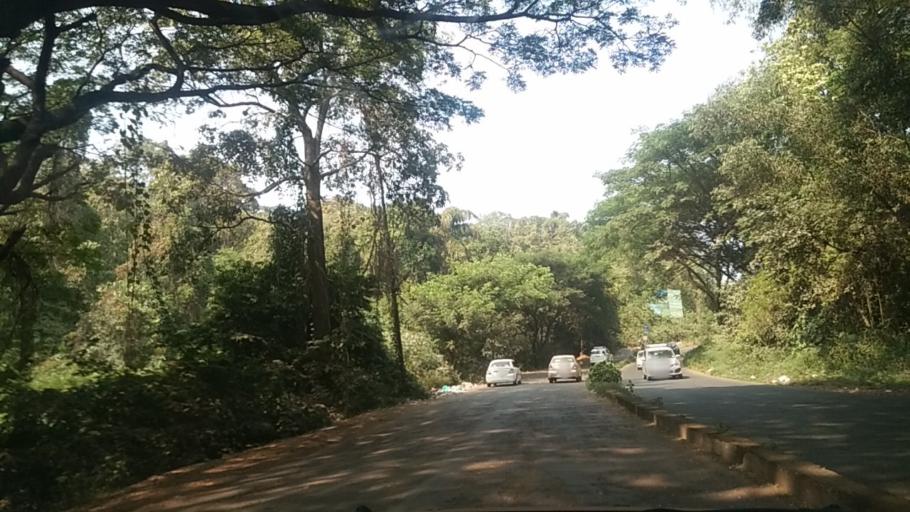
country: IN
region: Goa
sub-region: North Goa
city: Panaji
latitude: 15.5063
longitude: 73.8358
